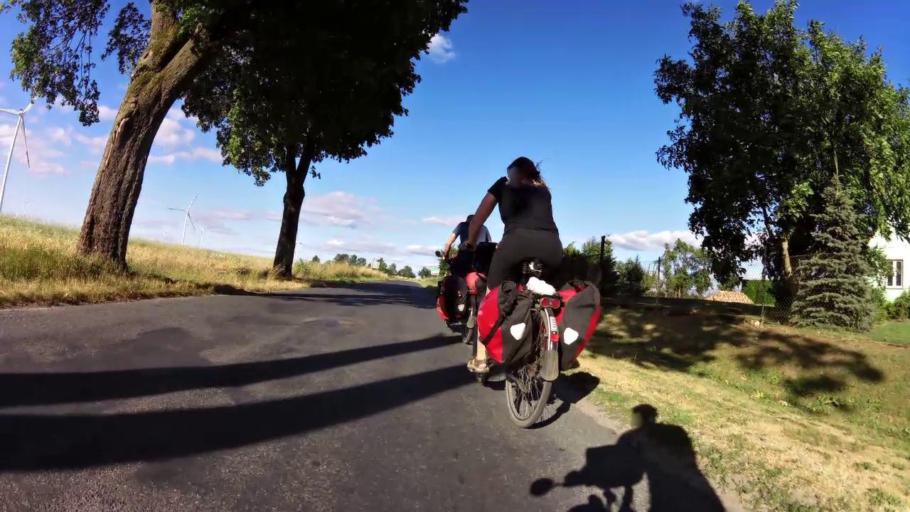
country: PL
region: West Pomeranian Voivodeship
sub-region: Powiat swidwinski
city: Swidwin
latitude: 53.6856
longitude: 15.7547
